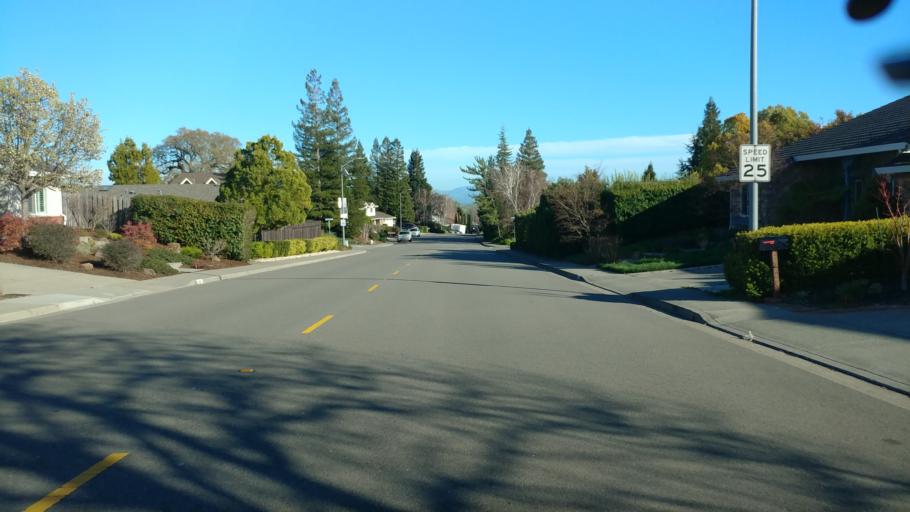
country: US
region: California
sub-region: Contra Costa County
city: San Ramon
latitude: 37.7555
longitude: -121.9707
